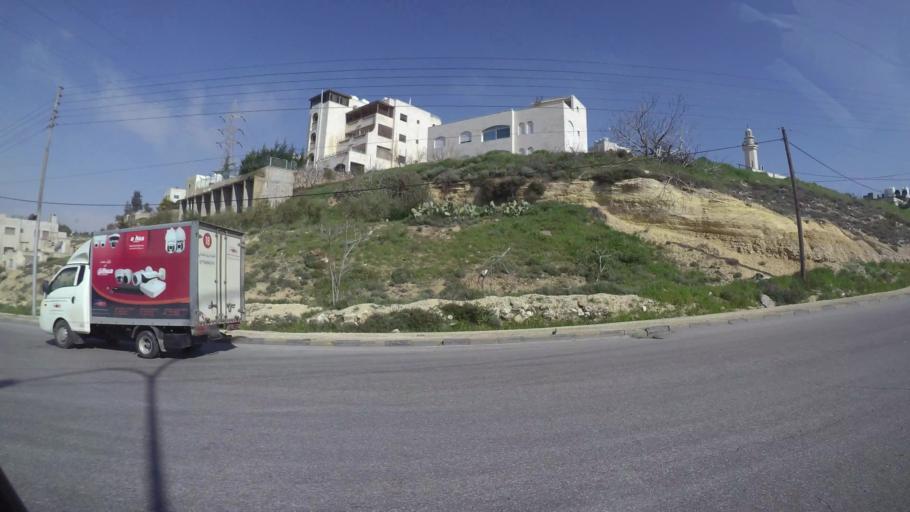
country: JO
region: Amman
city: Umm as Summaq
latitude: 31.8980
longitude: 35.8642
